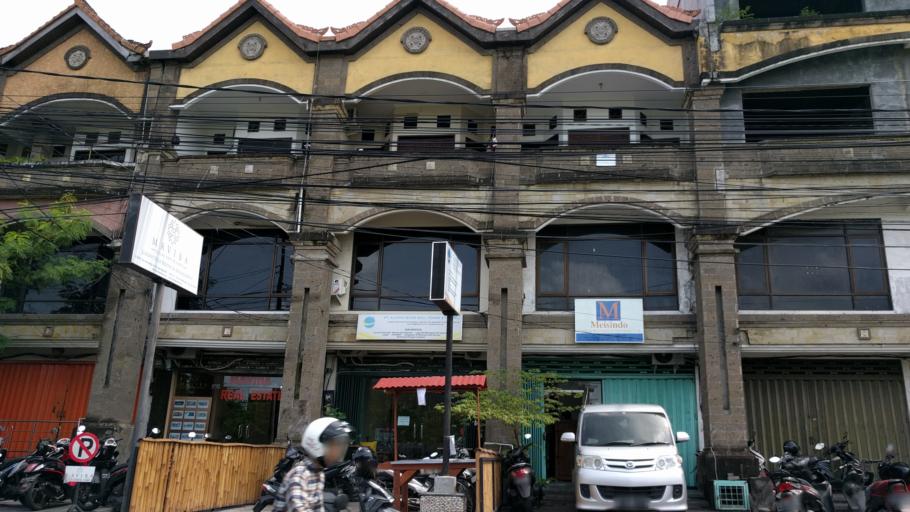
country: ID
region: Bali
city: Kuta
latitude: -8.6990
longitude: 115.1756
